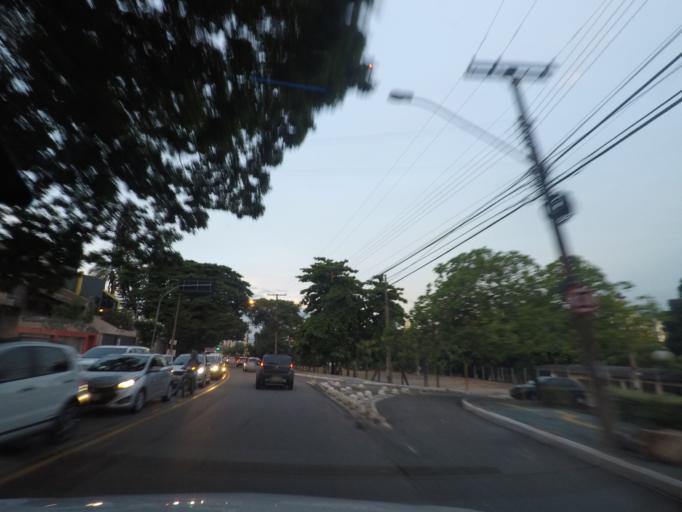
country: BR
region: Goias
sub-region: Goiania
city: Goiania
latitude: -16.7022
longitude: -49.2523
